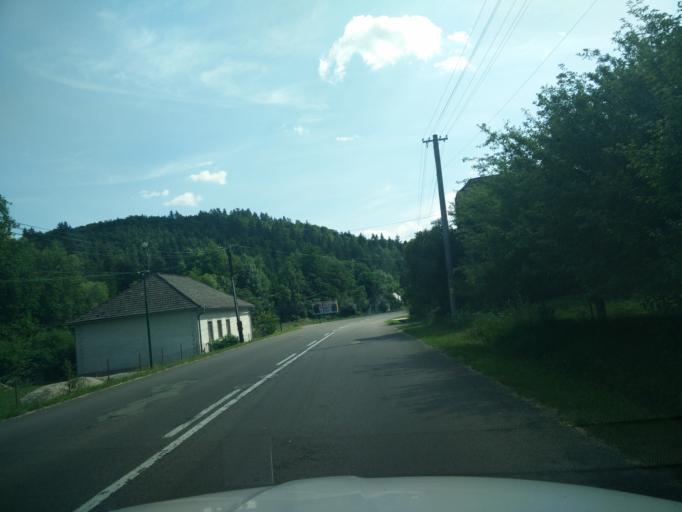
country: SK
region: Nitriansky
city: Prievidza
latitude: 48.9011
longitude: 18.6494
